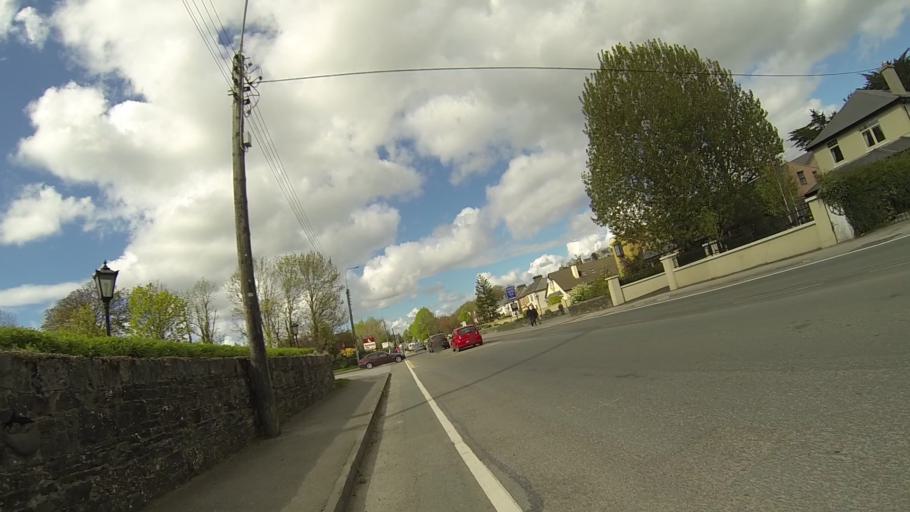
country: IE
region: Munster
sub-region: Ciarrai
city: Cill Airne
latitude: 52.0500
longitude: -9.5066
